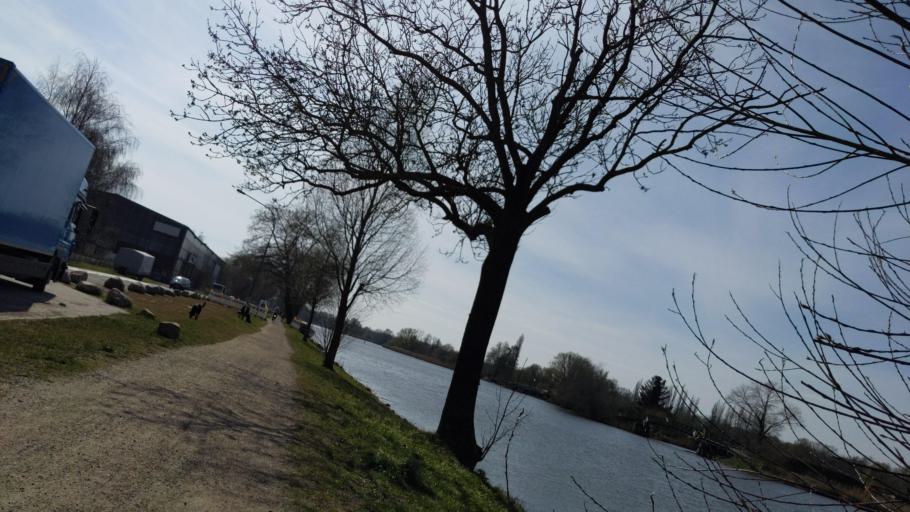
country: DE
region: Schleswig-Holstein
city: Luebeck
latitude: 53.8535
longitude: 10.6761
